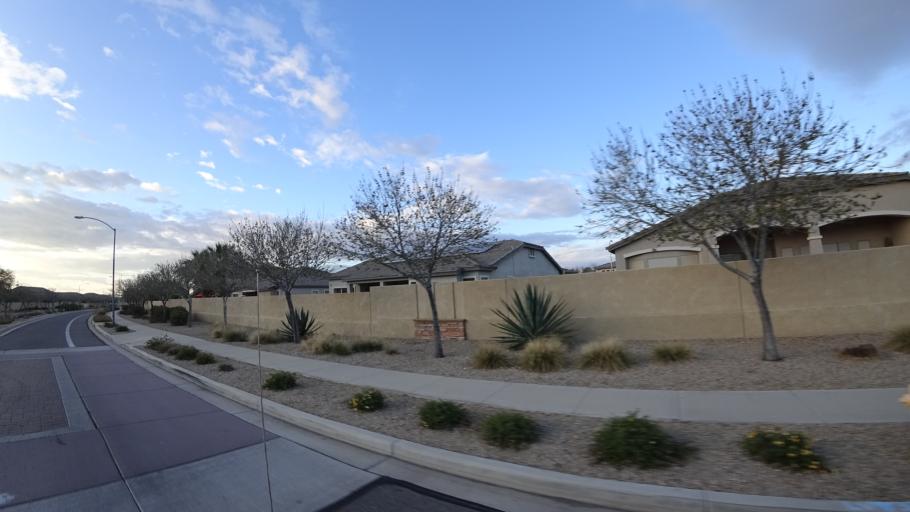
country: US
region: Arizona
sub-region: Maricopa County
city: Peoria
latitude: 33.5420
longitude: -112.2409
